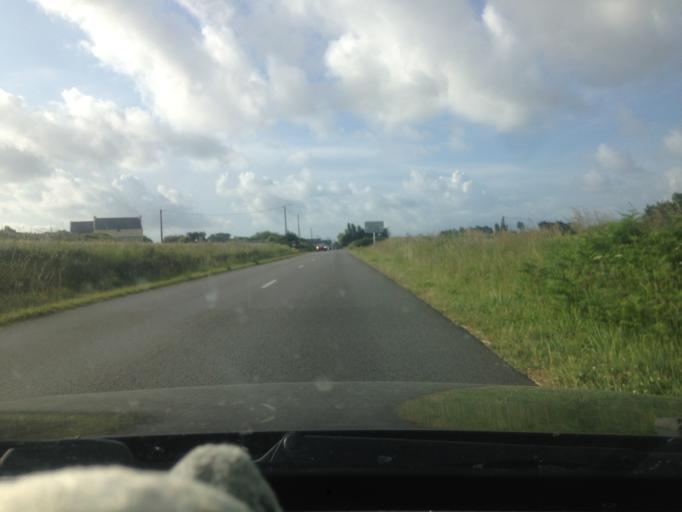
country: FR
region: Brittany
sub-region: Departement du Morbihan
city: Plouharnel
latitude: 47.6080
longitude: -3.1230
